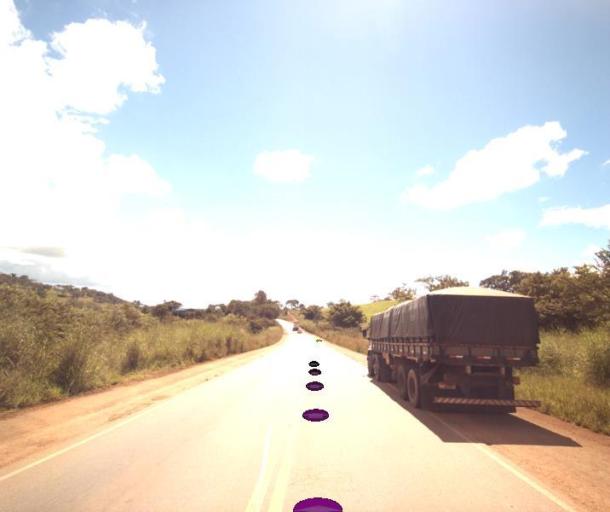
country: BR
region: Goias
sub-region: Anapolis
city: Anapolis
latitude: -16.1171
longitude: -49.0337
